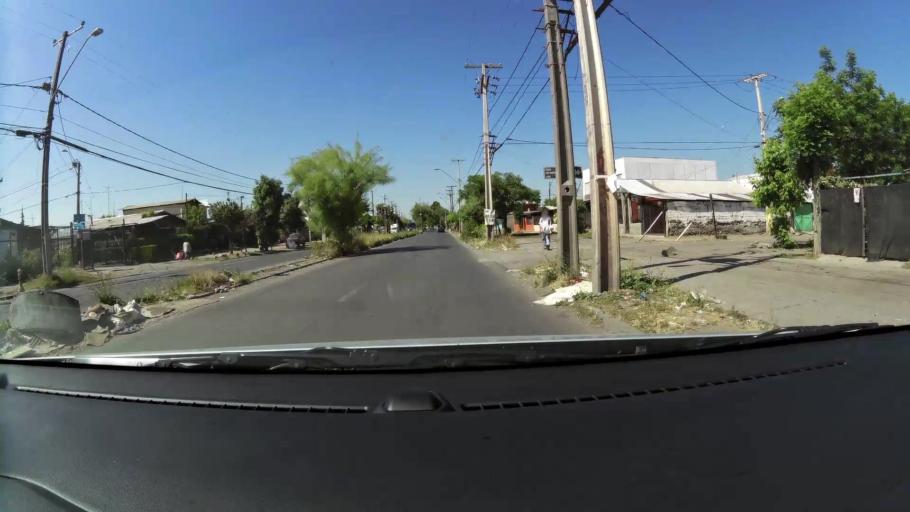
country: CL
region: Santiago Metropolitan
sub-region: Provincia de Santiago
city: La Pintana
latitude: -33.5570
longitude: -70.6555
